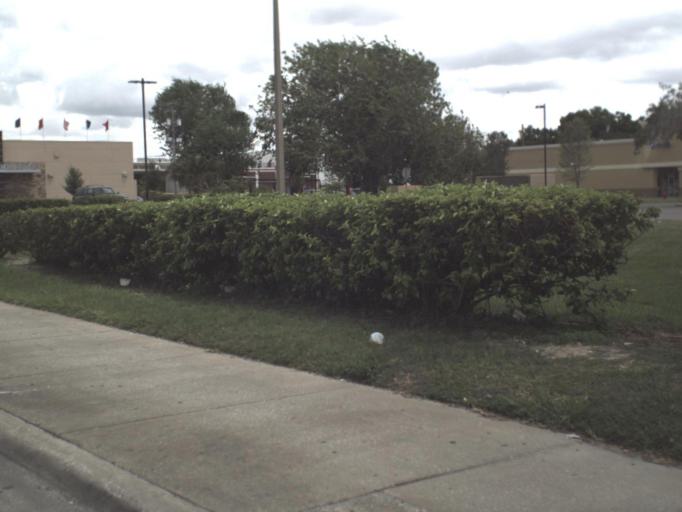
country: US
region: Florida
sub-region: Hillsborough County
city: East Lake-Orient Park
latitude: 27.9960
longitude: -82.4313
